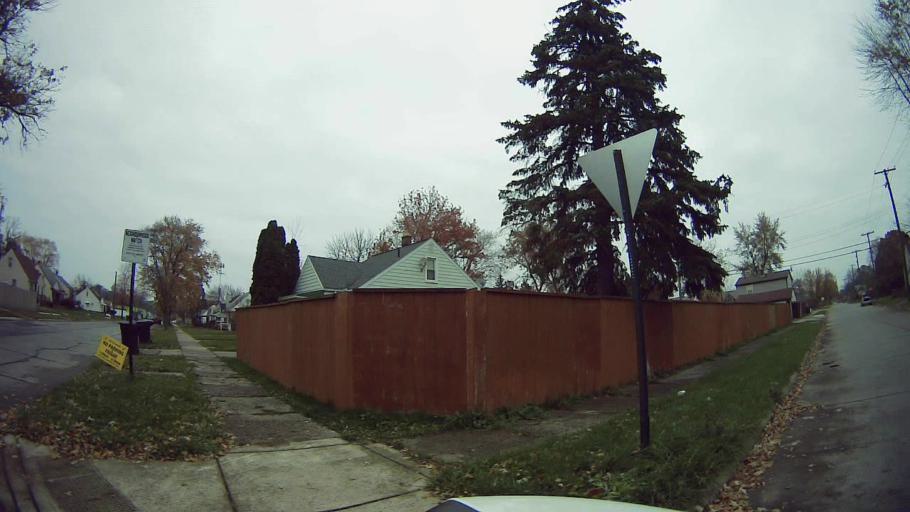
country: US
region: Michigan
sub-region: Wayne County
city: Dearborn Heights
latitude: 42.3557
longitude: -83.2370
